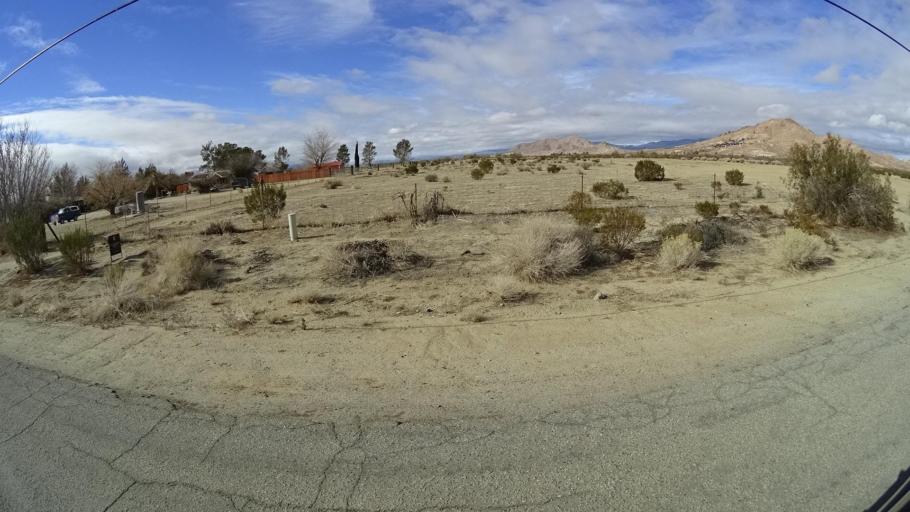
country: US
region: California
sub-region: Kern County
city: Rosamond
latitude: 34.8703
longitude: -118.2203
